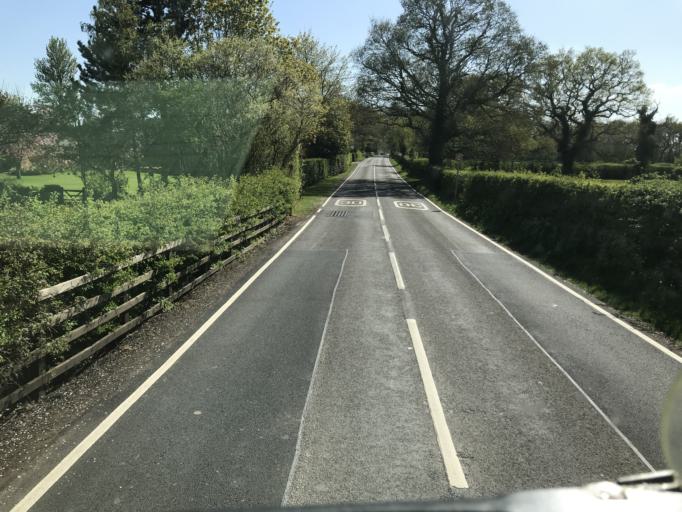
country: GB
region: England
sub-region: Cheshire East
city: Nantwich
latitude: 53.1095
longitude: -2.5121
